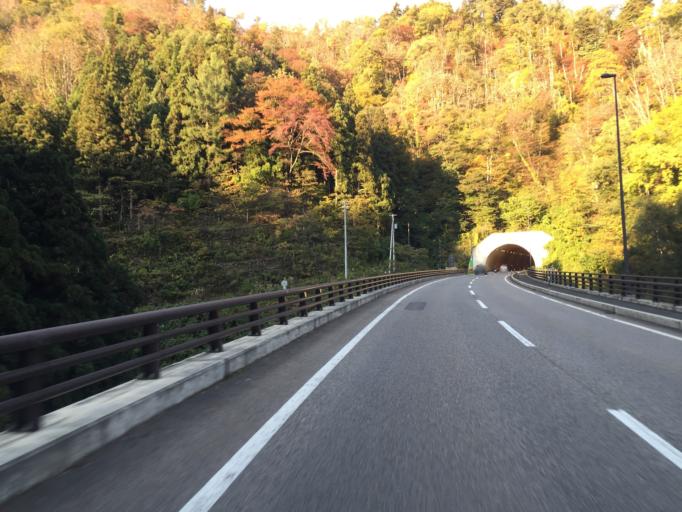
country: JP
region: Fukushima
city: Kitakata
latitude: 37.7458
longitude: 139.8872
